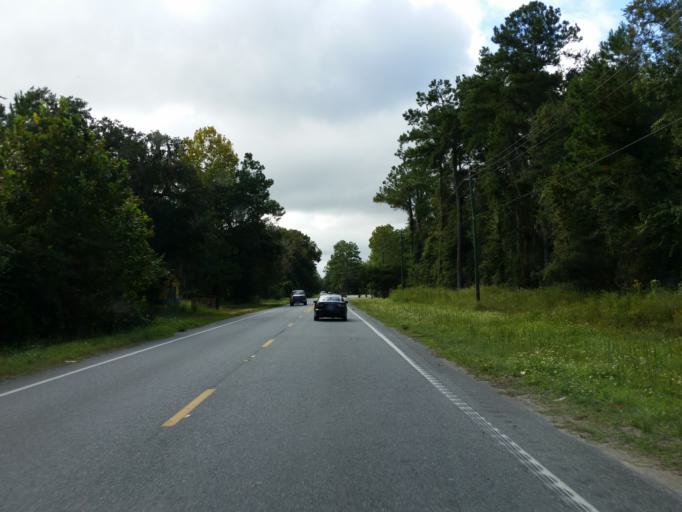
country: US
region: Florida
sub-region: Columbia County
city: Watertown
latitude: 30.1967
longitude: -82.6168
